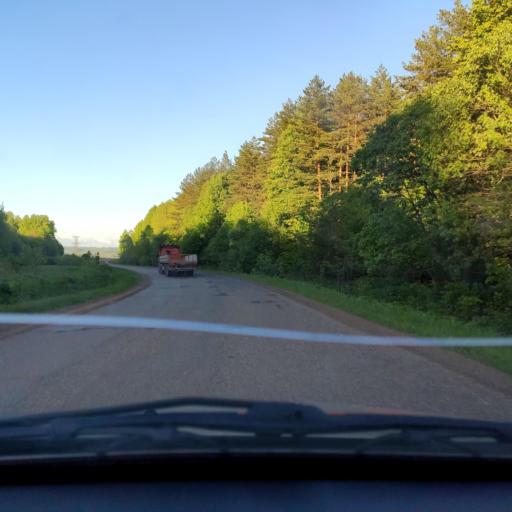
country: RU
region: Bashkortostan
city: Blagoveshchensk
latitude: 55.0410
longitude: 56.1351
